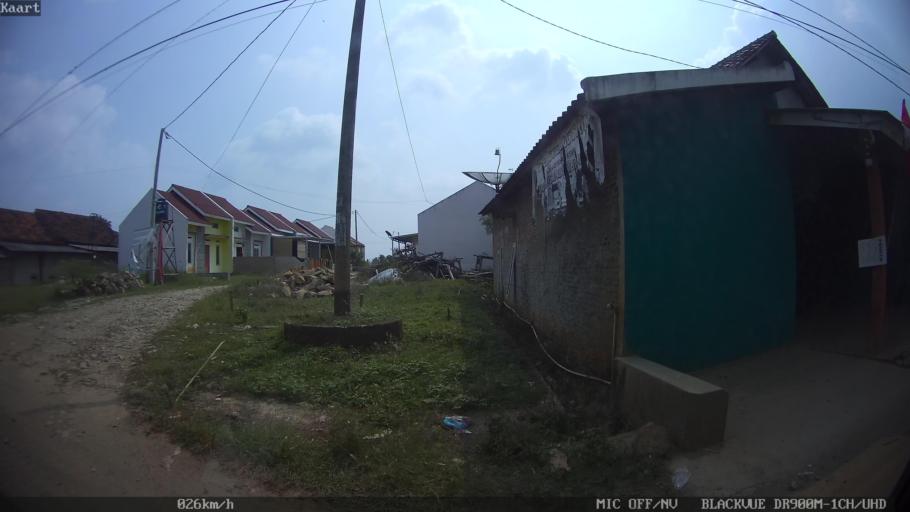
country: ID
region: Lampung
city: Gadingrejo
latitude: -5.3510
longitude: 105.0327
